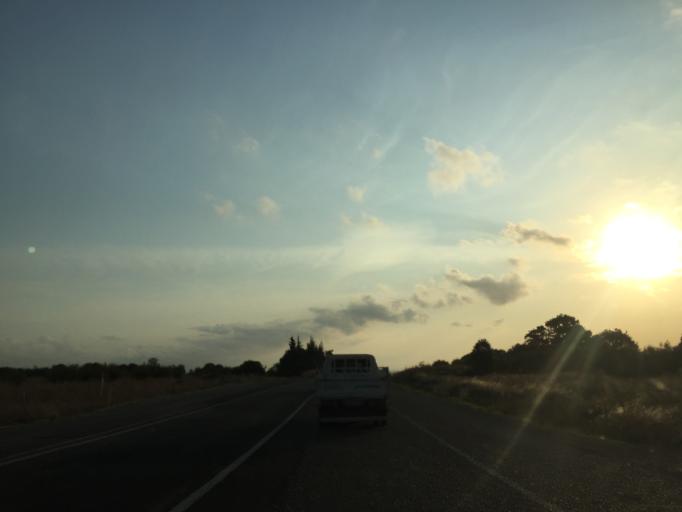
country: TR
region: Balikesir
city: Sevketiye
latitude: 40.1223
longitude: 27.8183
